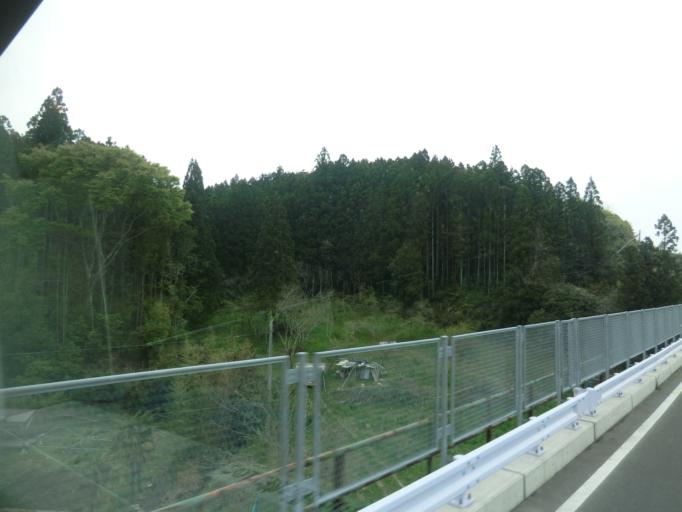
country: JP
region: Miyagi
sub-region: Oshika Gun
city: Onagawa Cho
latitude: 38.6507
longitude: 141.4429
